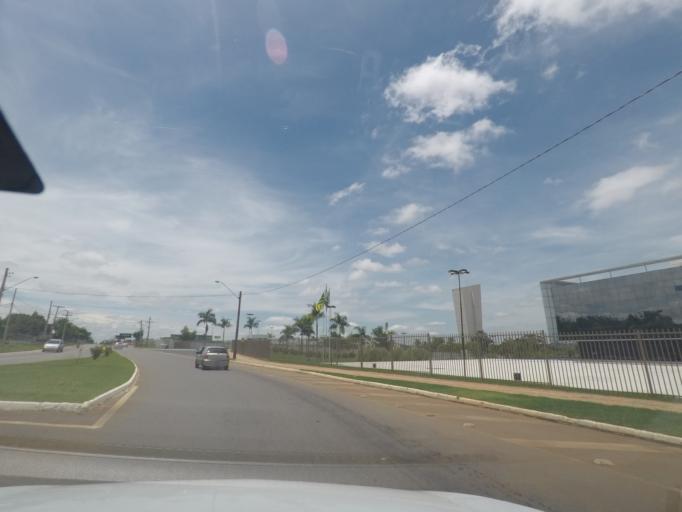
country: BR
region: Goias
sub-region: Goiania
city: Goiania
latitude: -16.6427
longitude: -49.2190
